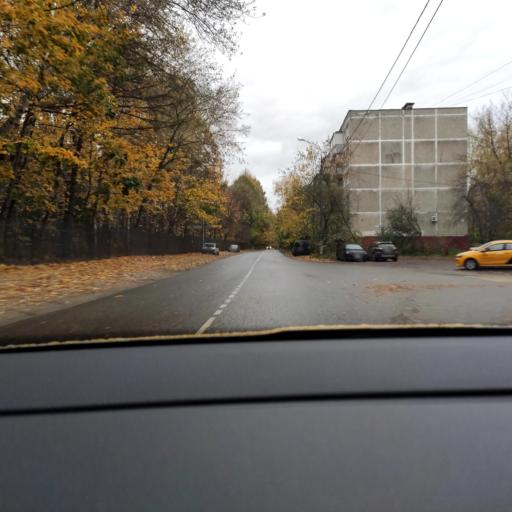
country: RU
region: Moskovskaya
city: Ivanteyevka
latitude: 55.9748
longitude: 37.8988
